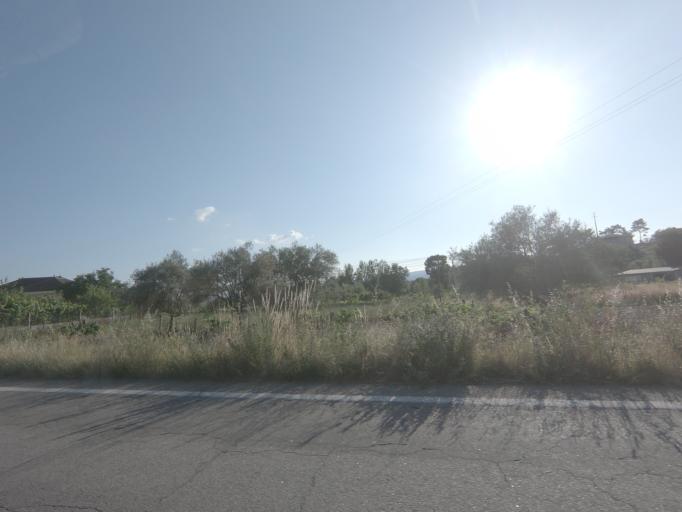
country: PT
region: Vila Real
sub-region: Chaves
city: Chaves
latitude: 41.7929
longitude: -7.4233
